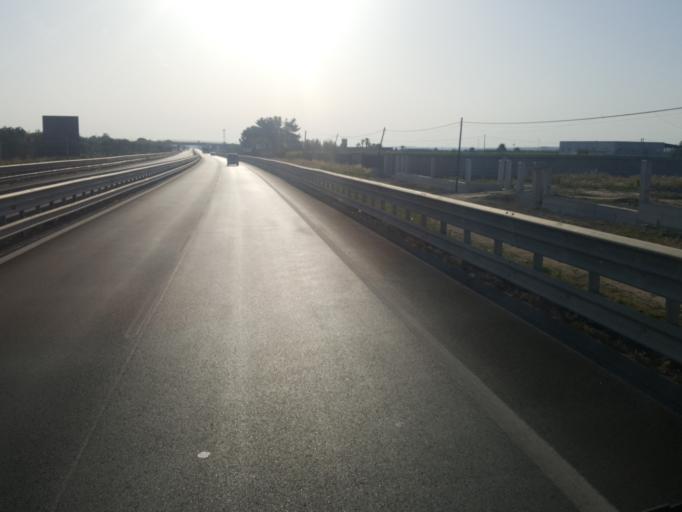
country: IT
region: Apulia
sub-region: Provincia di Foggia
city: Cerignola
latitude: 41.2637
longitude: 15.9303
